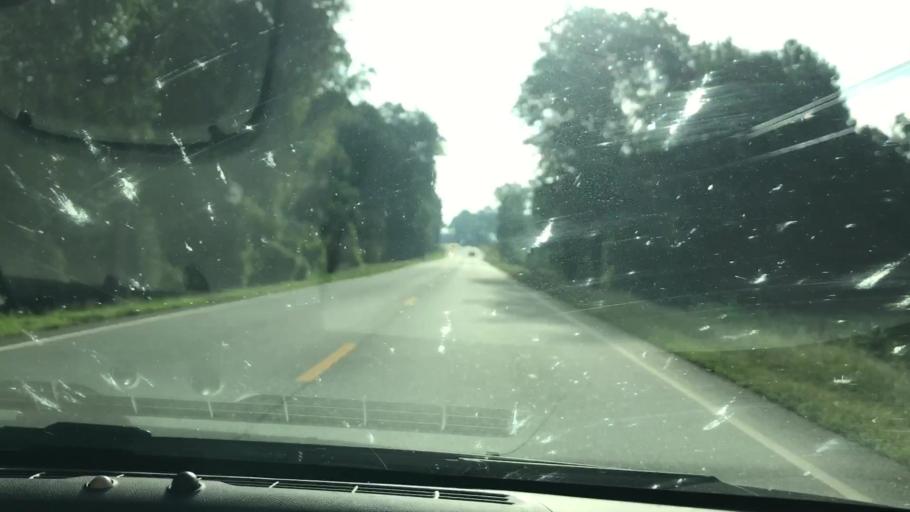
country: US
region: Georgia
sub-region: Terrell County
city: Dawson
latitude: 31.7694
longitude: -84.4664
